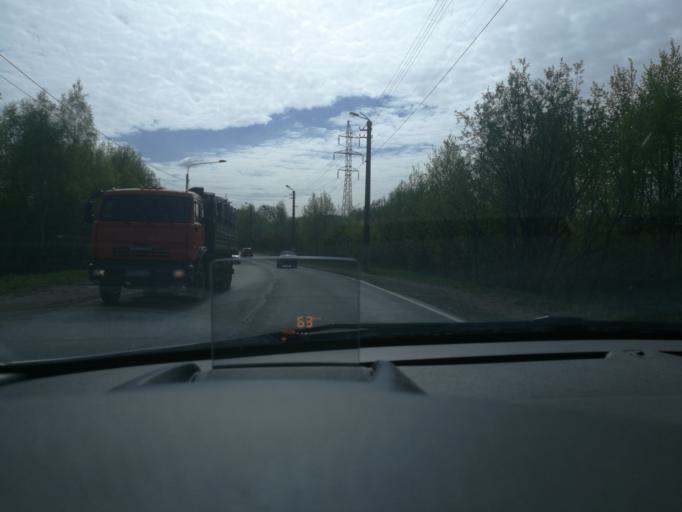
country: RU
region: Arkhangelskaya
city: Arkhangel'sk
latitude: 64.5985
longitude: 40.5565
